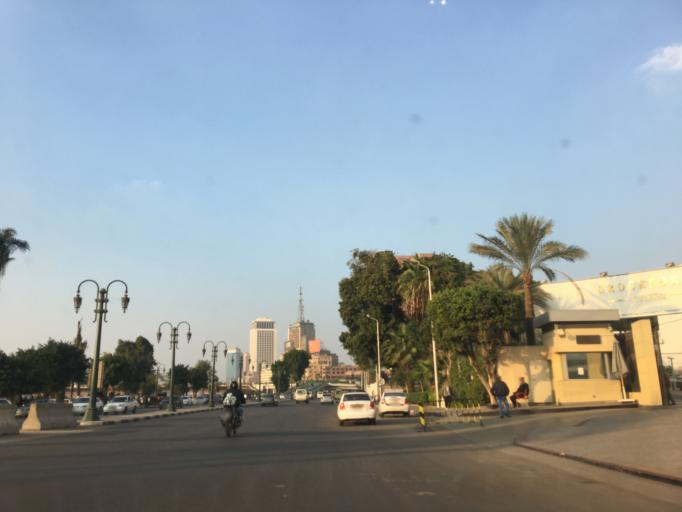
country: EG
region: Muhafazat al Qahirah
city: Cairo
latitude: 30.0459
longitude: 31.2317
